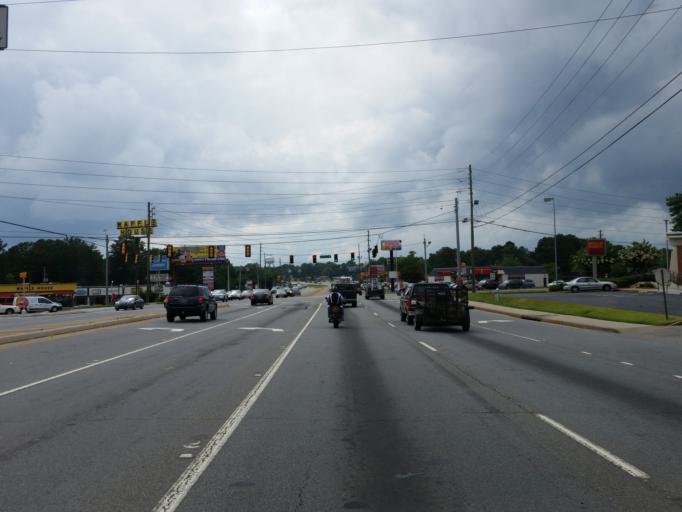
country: US
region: Georgia
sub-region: Cherokee County
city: Woodstock
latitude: 34.0879
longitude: -84.5761
